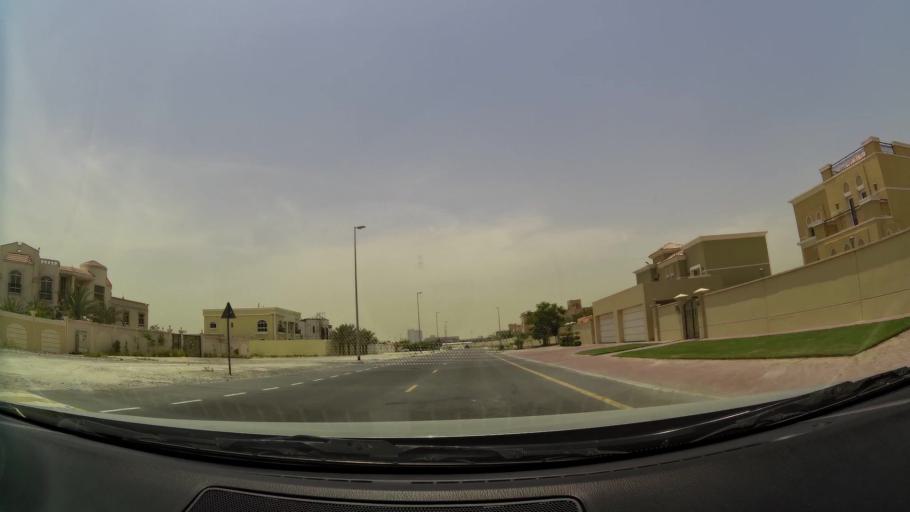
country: AE
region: Dubai
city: Dubai
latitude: 25.0848
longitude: 55.2253
